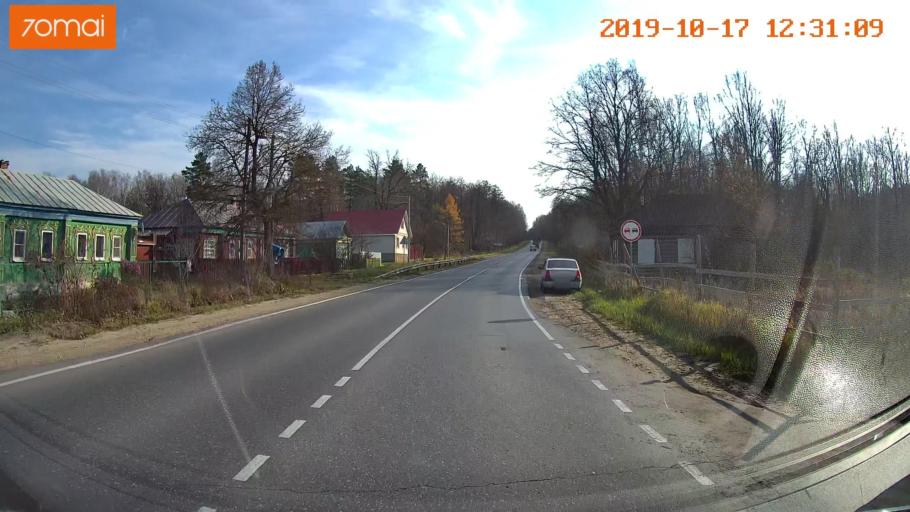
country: RU
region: Rjazan
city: Syntul
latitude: 54.9708
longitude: 41.3305
